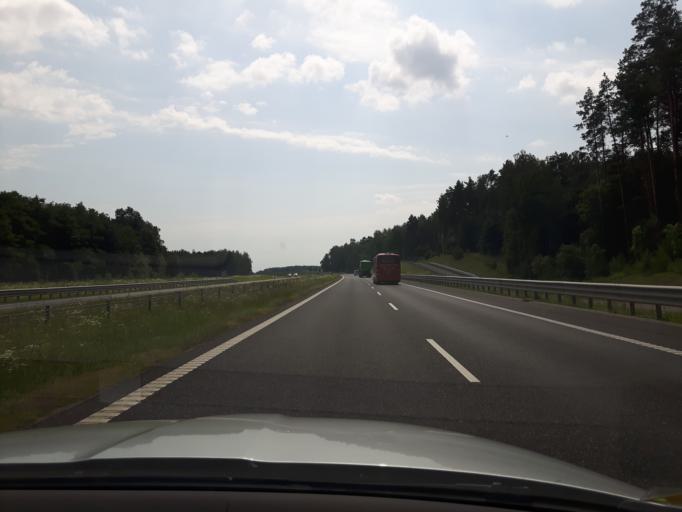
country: PL
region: Warmian-Masurian Voivodeship
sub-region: Powiat olsztynski
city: Olsztynek
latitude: 53.4598
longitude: 20.3215
